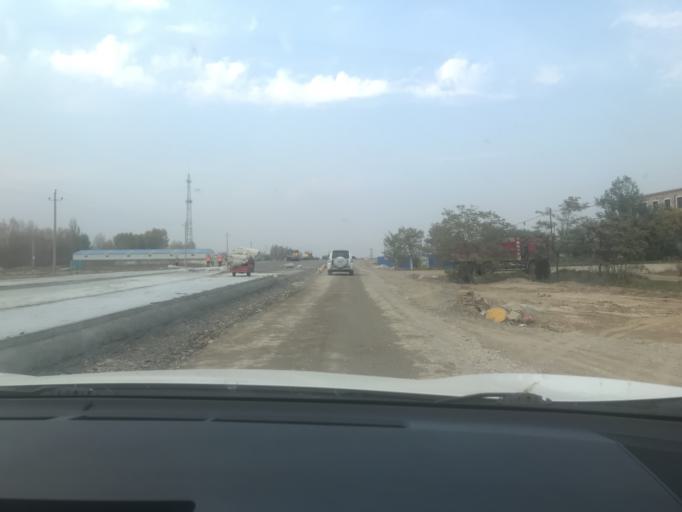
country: CN
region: Gansu Sheng
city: Gulang
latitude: 37.5145
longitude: 102.9009
